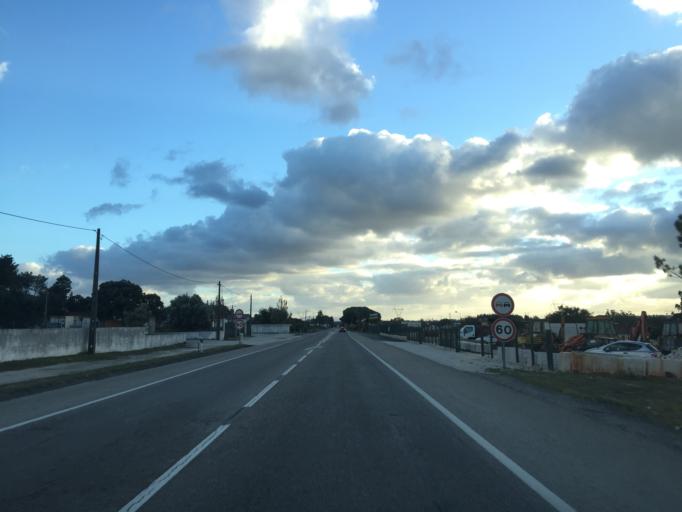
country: PT
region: Leiria
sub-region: Alcobaca
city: Benedita
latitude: 39.4487
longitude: -8.9504
